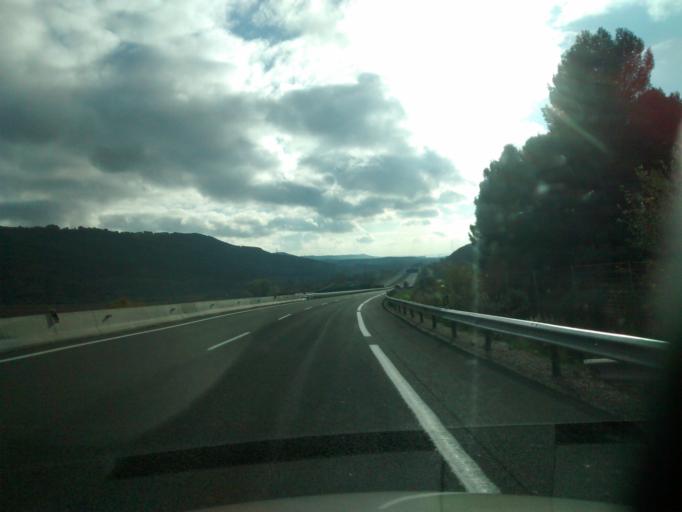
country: ES
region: Castille-La Mancha
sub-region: Provincia de Guadalajara
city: Tortola de Henares
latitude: 40.6788
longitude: -3.0968
